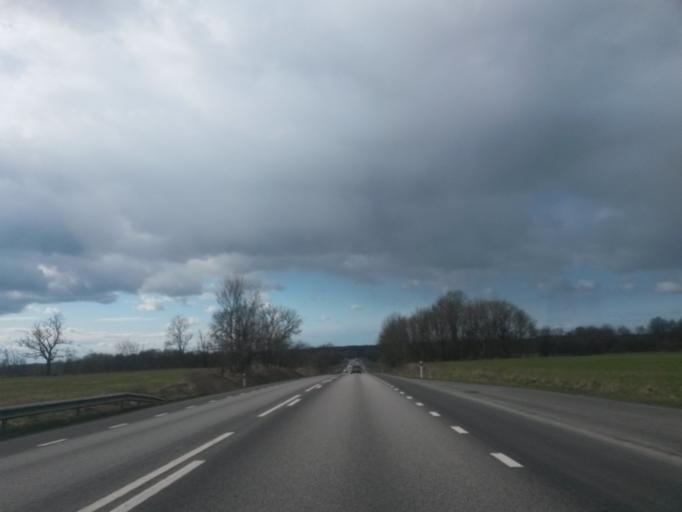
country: SE
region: Vaestra Goetaland
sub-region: Skara Kommun
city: Axvall
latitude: 58.3858
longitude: 13.6613
